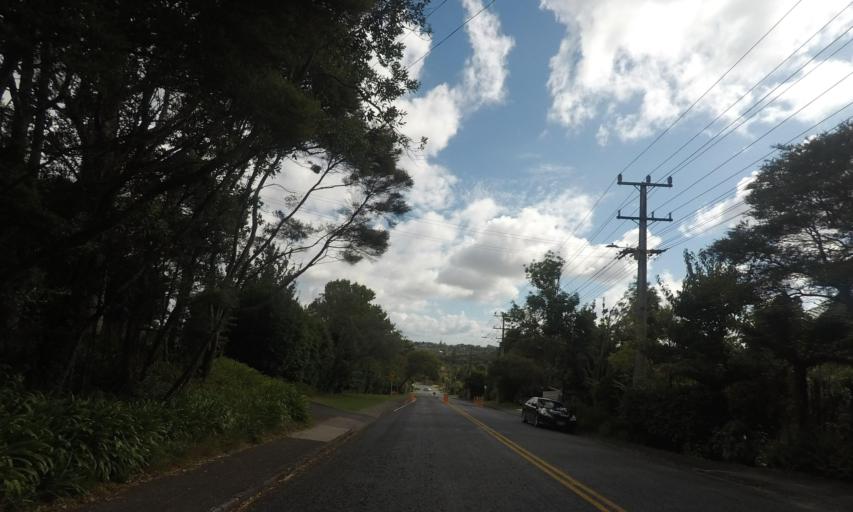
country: NZ
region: Auckland
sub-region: Auckland
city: Titirangi
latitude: -36.9342
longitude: 174.6550
